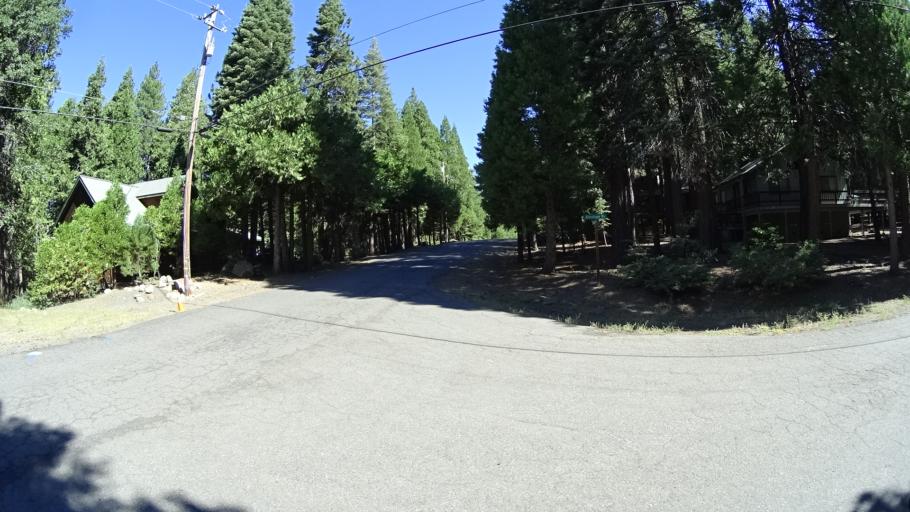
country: US
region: California
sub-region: Calaveras County
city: Arnold
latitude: 38.2973
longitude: -120.2704
